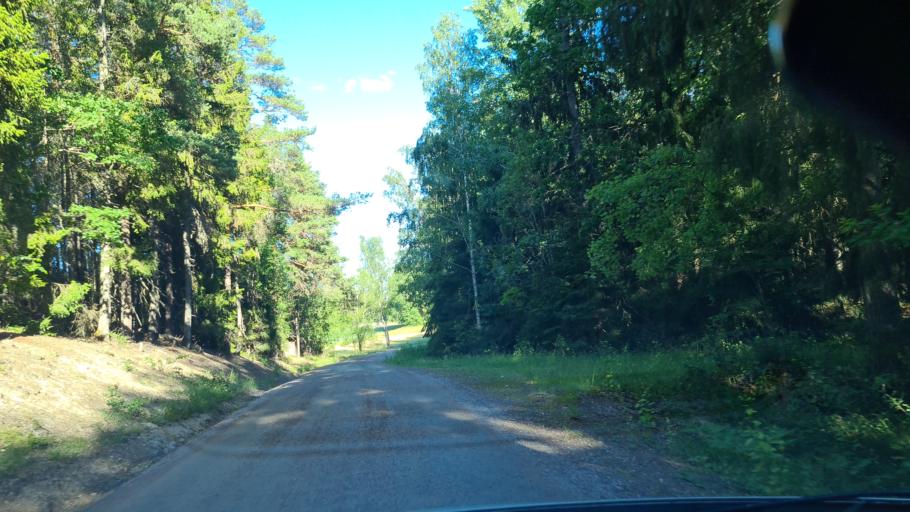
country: SE
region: Soedermanland
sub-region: Nykopings Kommun
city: Nykoping
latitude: 58.9209
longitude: 17.0327
